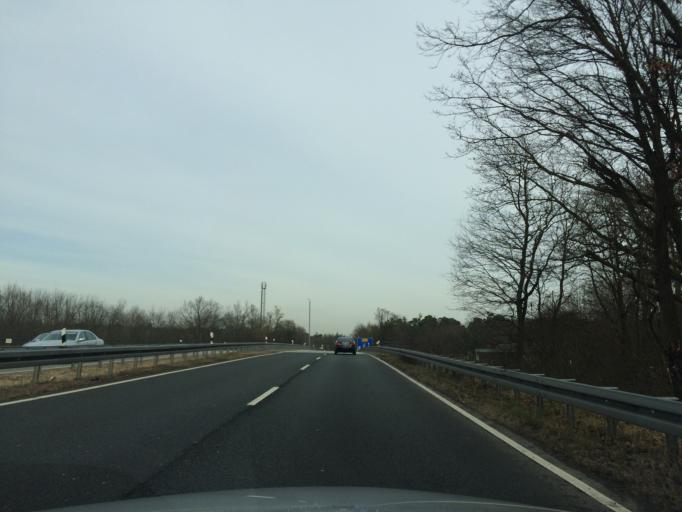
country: DE
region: Hesse
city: Niederrad
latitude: 50.0579
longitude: 8.6481
